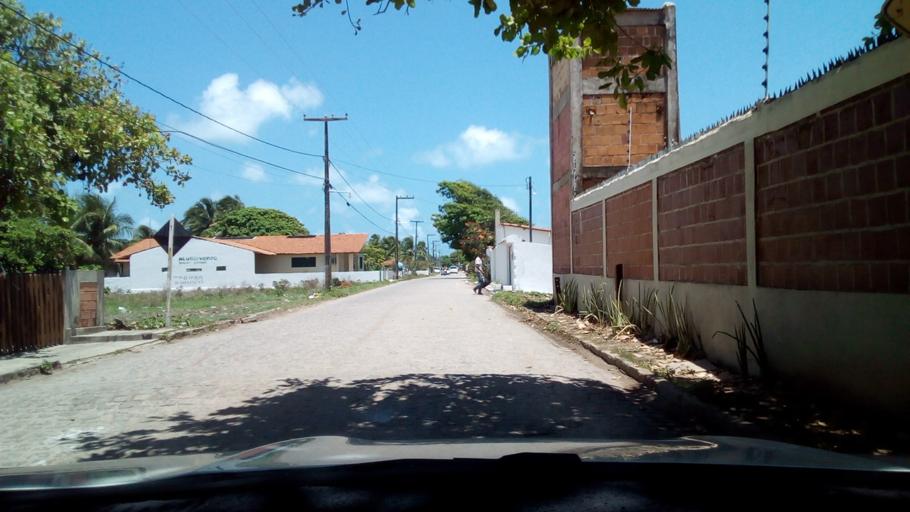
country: BR
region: Paraiba
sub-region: Pitimbu
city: Pitimbu
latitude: -7.5153
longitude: -34.8123
